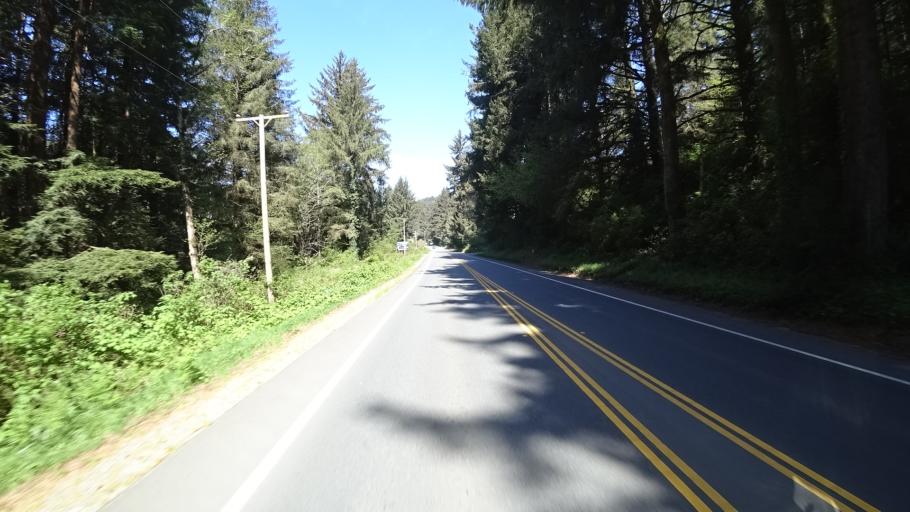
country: US
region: California
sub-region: Del Norte County
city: Bertsch-Oceanview
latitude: 41.5799
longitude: -124.0774
